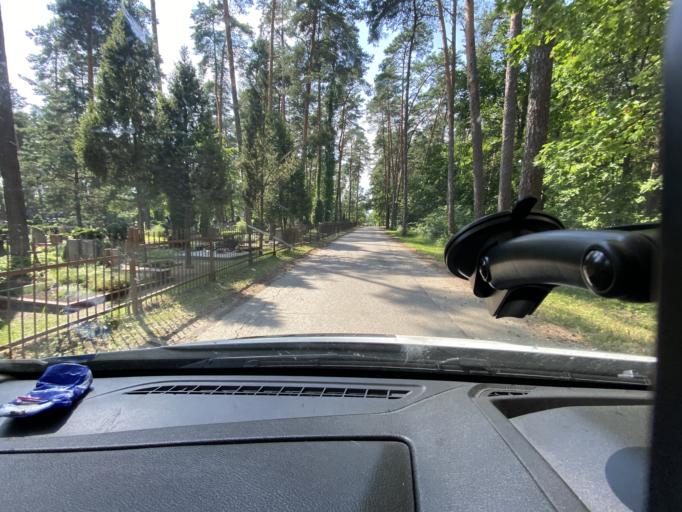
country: LT
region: Kauno apskritis
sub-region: Kauno rajonas
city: Karmelava
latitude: 54.9741
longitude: 24.0487
